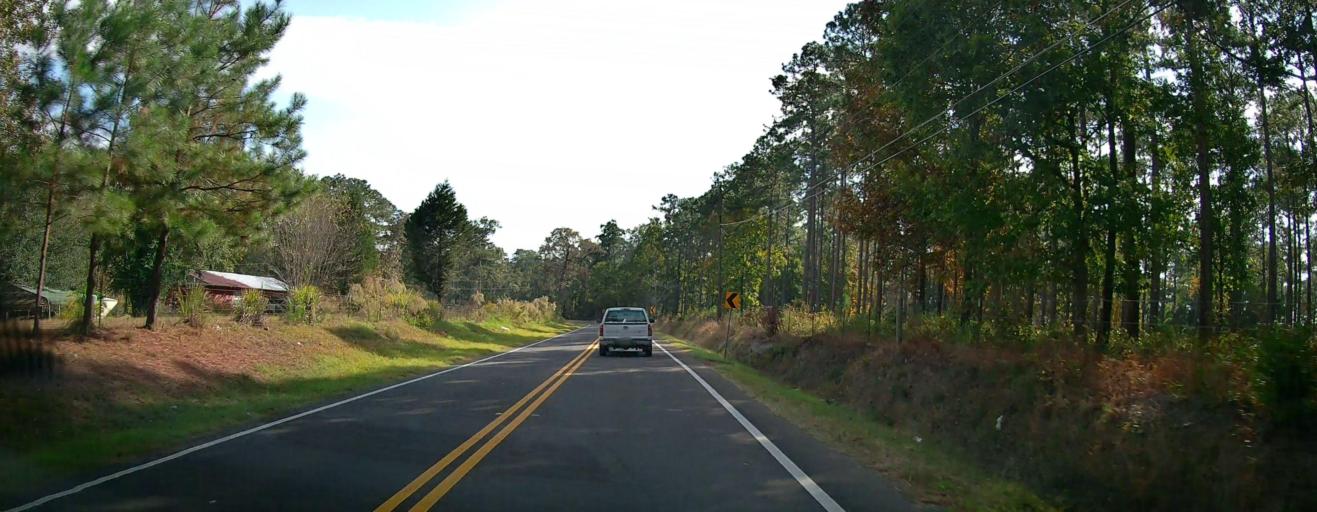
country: US
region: Georgia
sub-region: Thomas County
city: Thomasville
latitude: 30.8786
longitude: -84.0067
